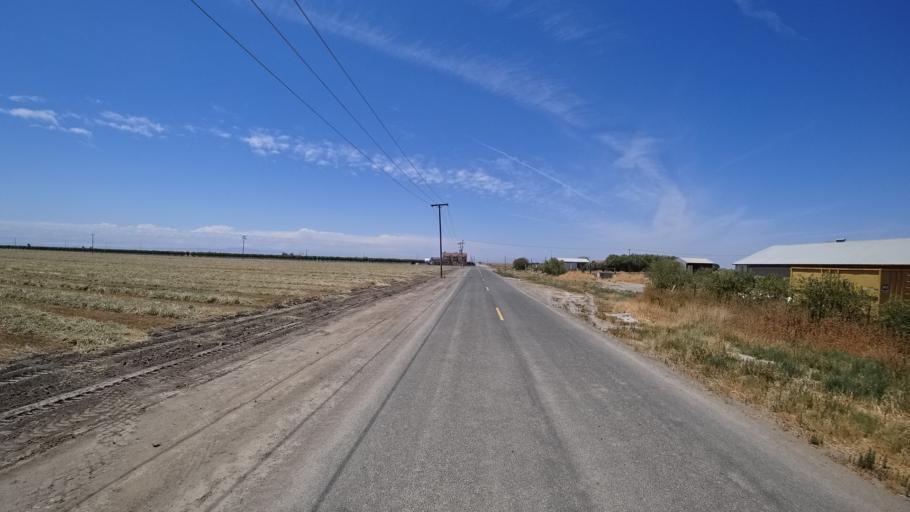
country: US
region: California
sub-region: Kings County
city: Stratford
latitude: 36.2331
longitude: -119.7967
